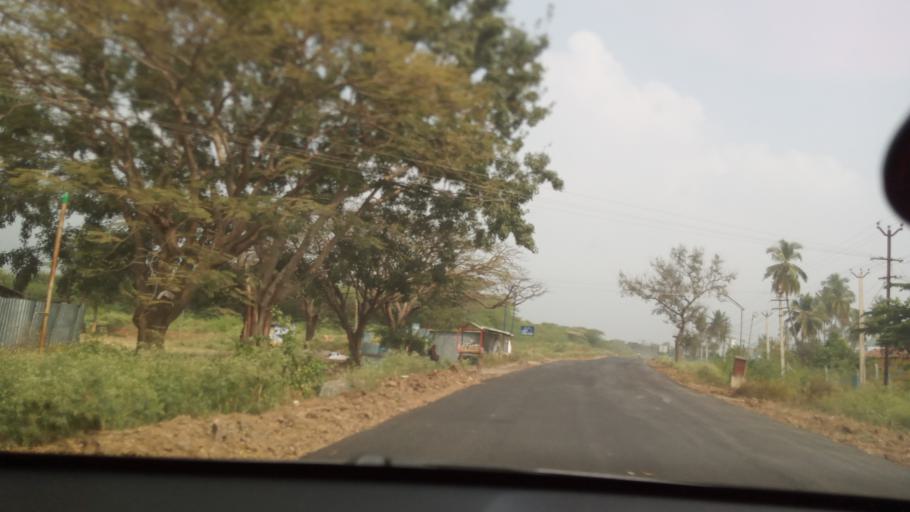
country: IN
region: Tamil Nadu
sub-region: Erode
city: Sathyamangalam
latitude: 11.5405
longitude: 77.1386
